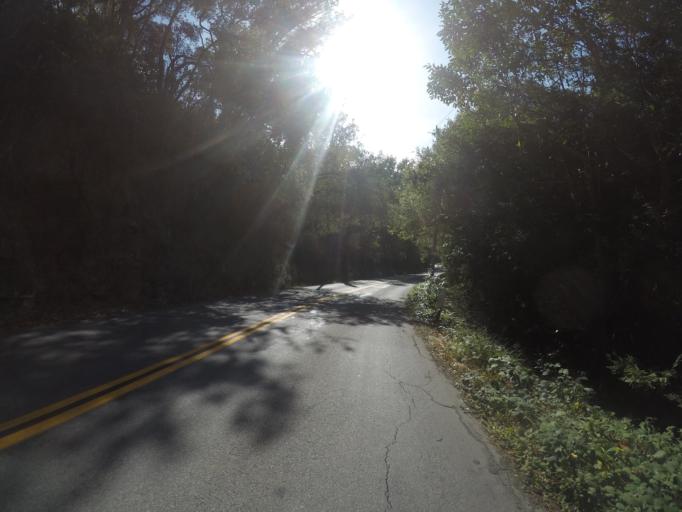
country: US
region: California
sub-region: Santa Cruz County
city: Soquel
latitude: 37.0002
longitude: -121.9702
